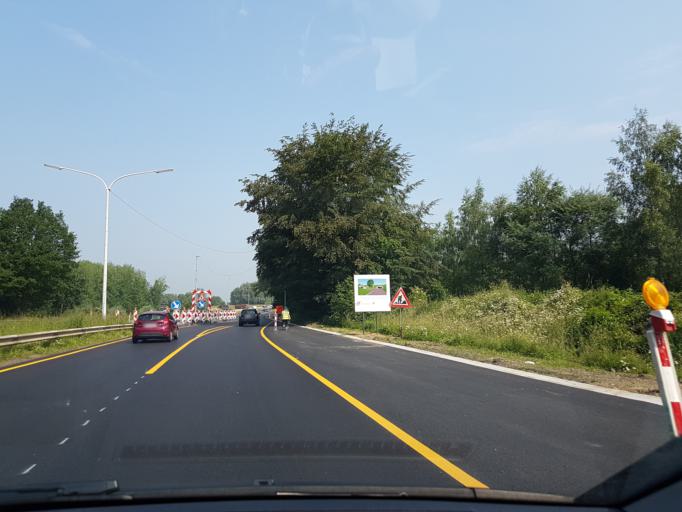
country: BE
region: Flanders
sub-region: Provincie Oost-Vlaanderen
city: Aalst
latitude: 50.9311
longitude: 4.0171
